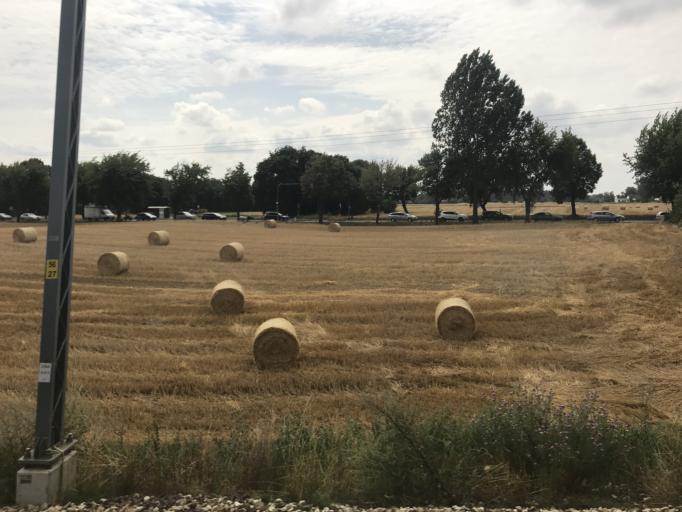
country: PL
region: Greater Poland Voivodeship
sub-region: Powiat gnieznienski
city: Trzemeszno
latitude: 52.5592
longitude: 17.7671
